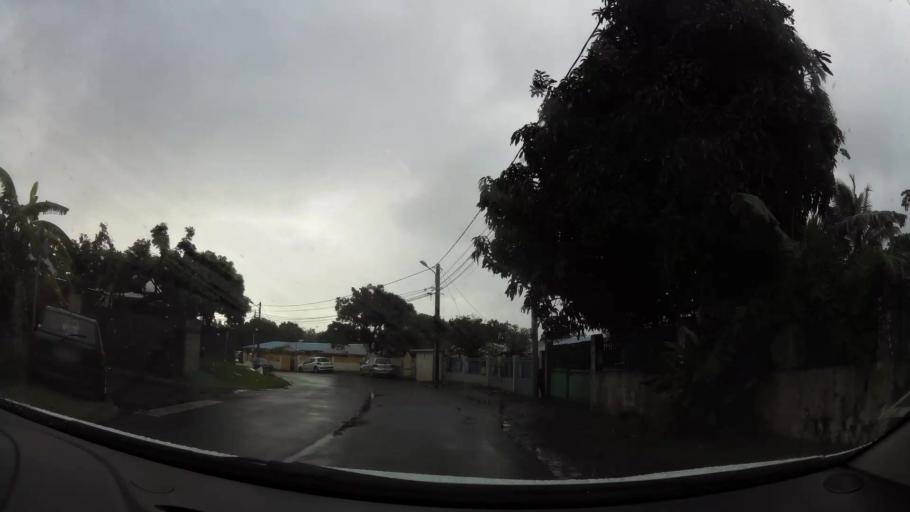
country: RE
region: Reunion
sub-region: Reunion
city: Saint-Andre
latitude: -20.9737
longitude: 55.6529
